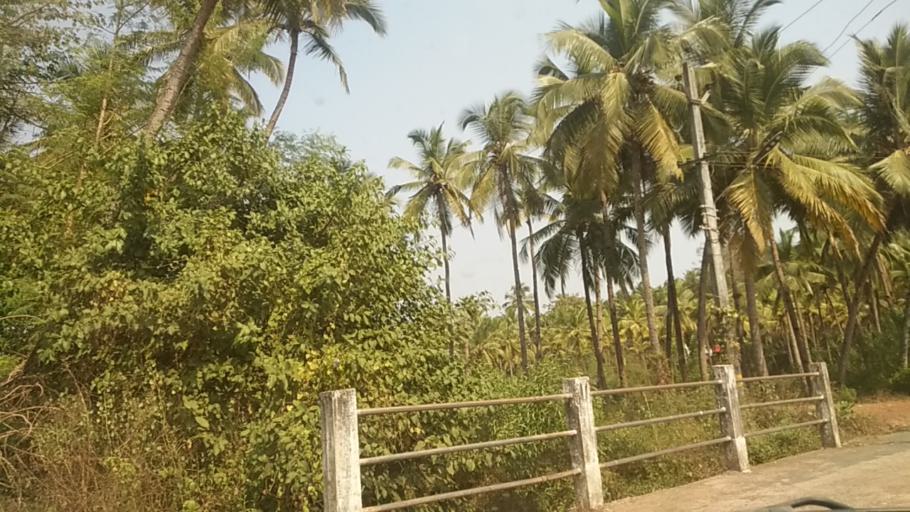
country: IN
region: Goa
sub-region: South Goa
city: Cavelossim
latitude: 15.1360
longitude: 73.9557
